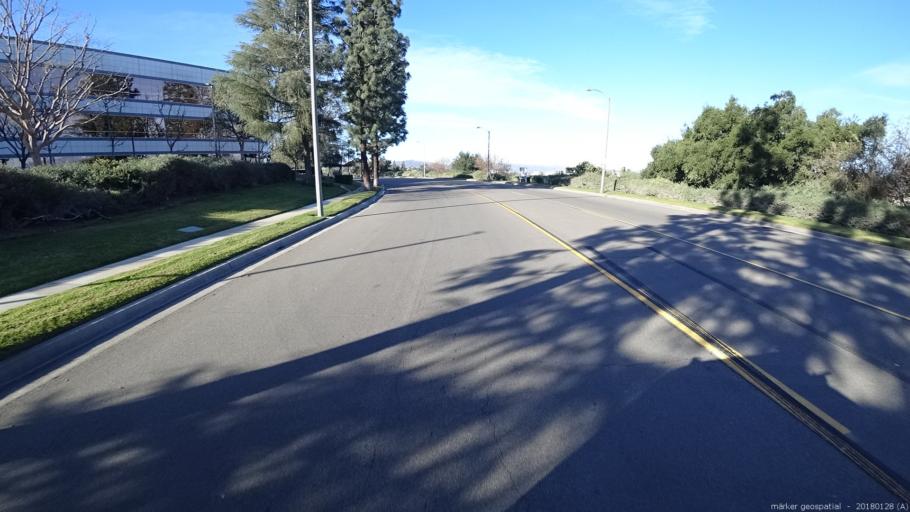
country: US
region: California
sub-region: Los Angeles County
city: Diamond Bar
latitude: 33.9990
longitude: -117.8325
